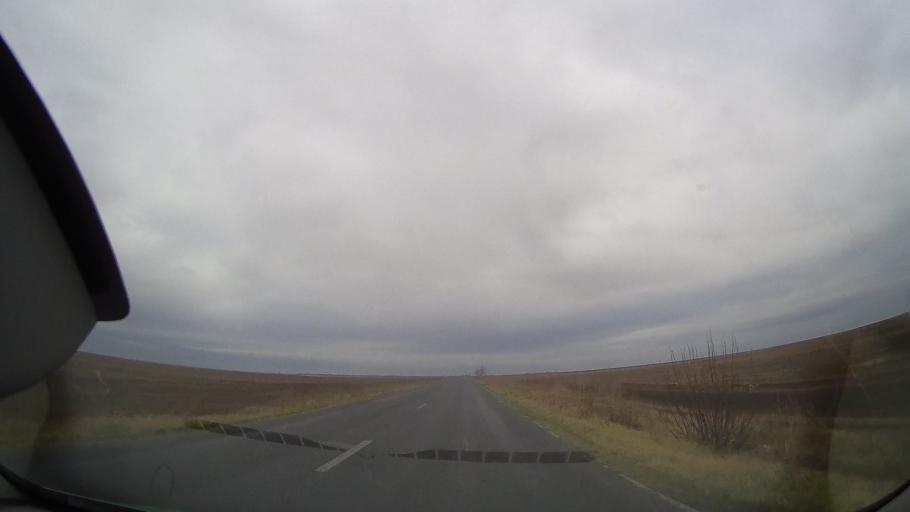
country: RO
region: Buzau
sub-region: Comuna Padina
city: Padina
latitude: 44.8110
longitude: 27.1267
